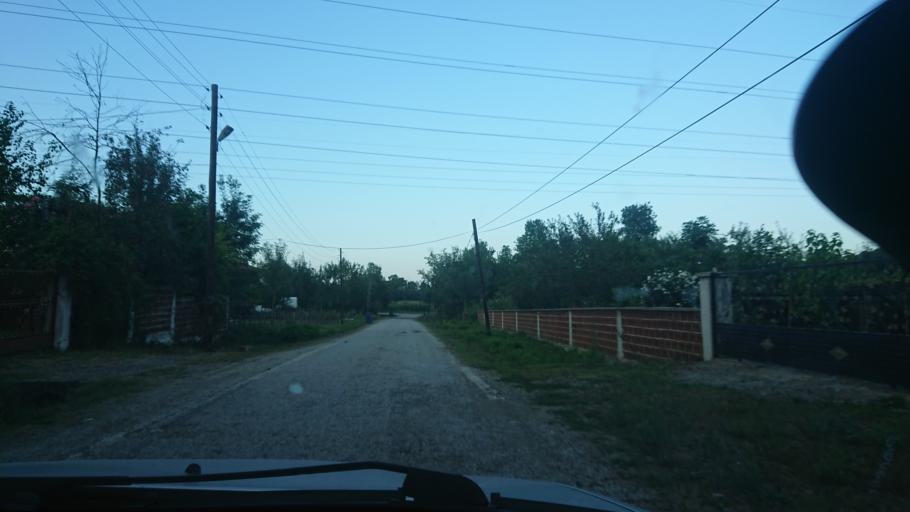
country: TR
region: Samsun
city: Dikbiyik
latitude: 41.1778
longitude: 36.5457
